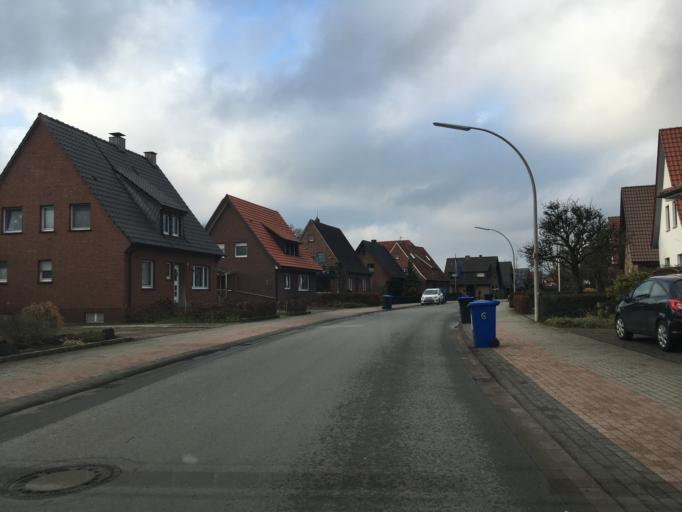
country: DE
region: North Rhine-Westphalia
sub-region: Regierungsbezirk Munster
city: Gescher
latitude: 51.9489
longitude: 7.0013
